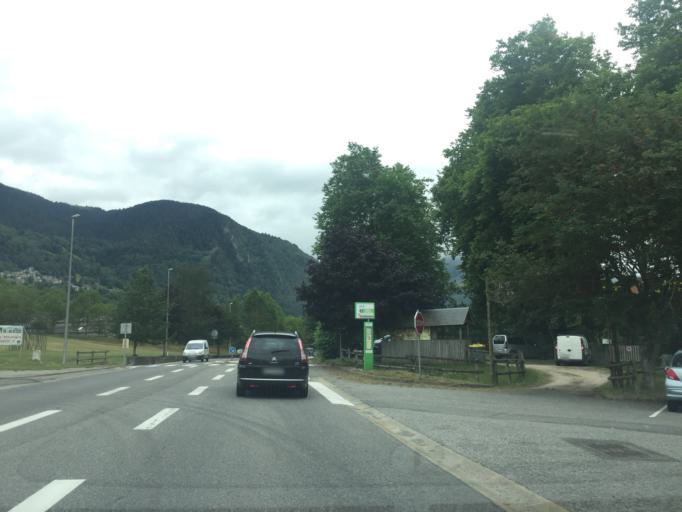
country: FR
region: Midi-Pyrenees
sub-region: Departement des Hautes-Pyrenees
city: Saint-Lary-Soulan
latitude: 42.8501
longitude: 0.3467
